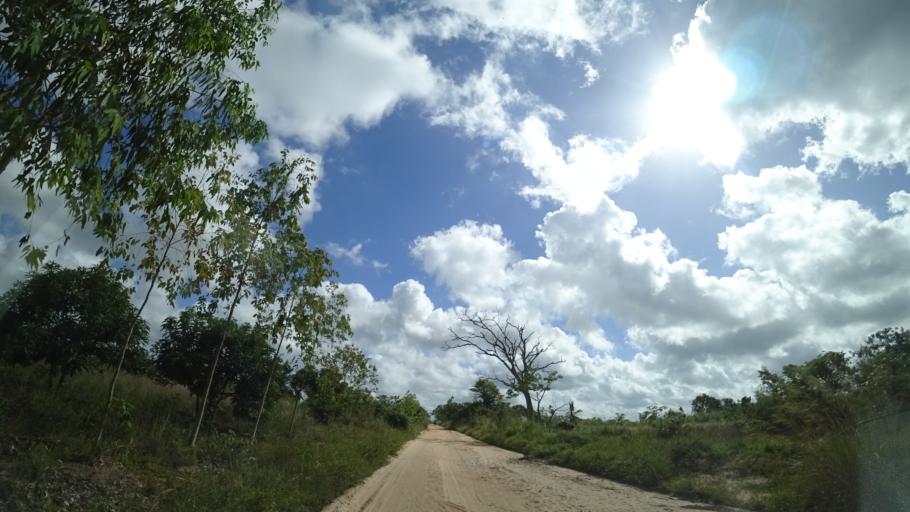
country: MZ
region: Sofala
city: Dondo
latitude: -19.4018
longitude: 34.7091
